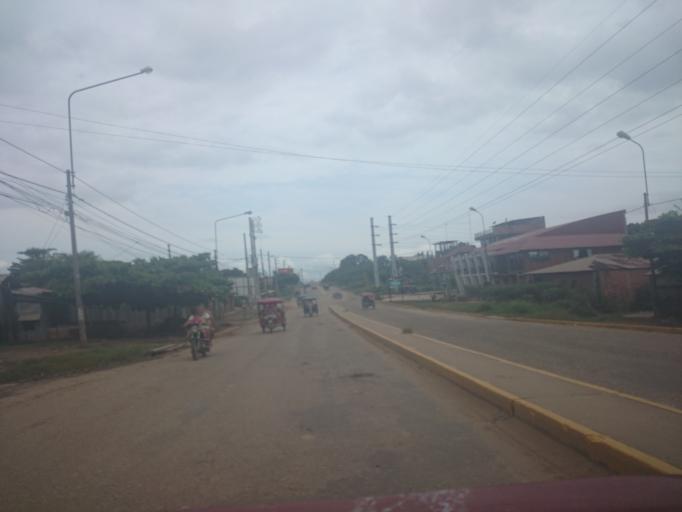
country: PE
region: Ucayali
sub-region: Provincia de Coronel Portillo
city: Pucallpa
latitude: -8.3718
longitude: -74.5529
